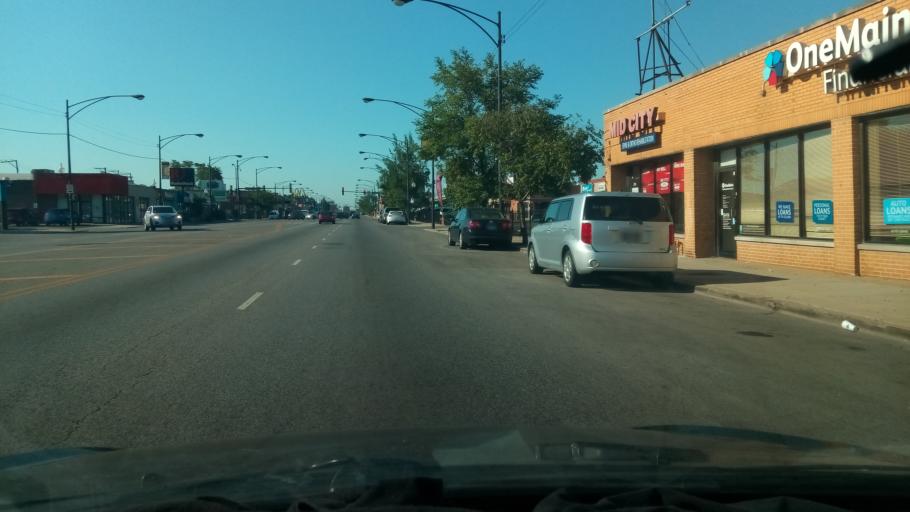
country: US
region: Illinois
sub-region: Cook County
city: Hometown
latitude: 41.7735
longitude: -87.7228
